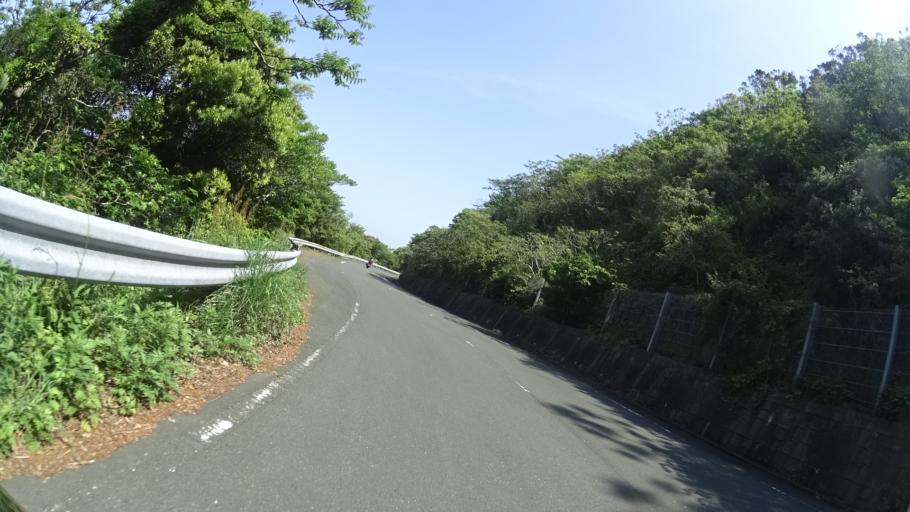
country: JP
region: Oita
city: Tsukumiura
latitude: 33.3568
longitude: 132.0333
